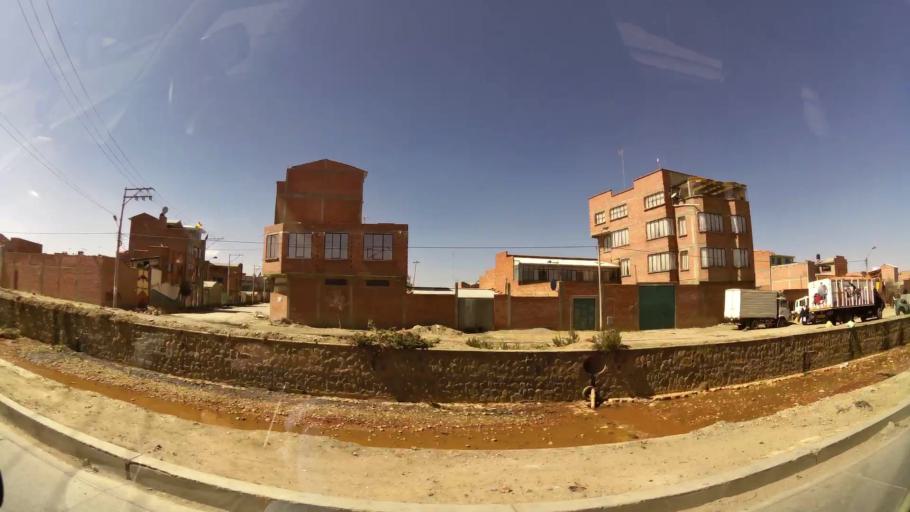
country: BO
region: La Paz
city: La Paz
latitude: -16.4997
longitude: -68.2082
